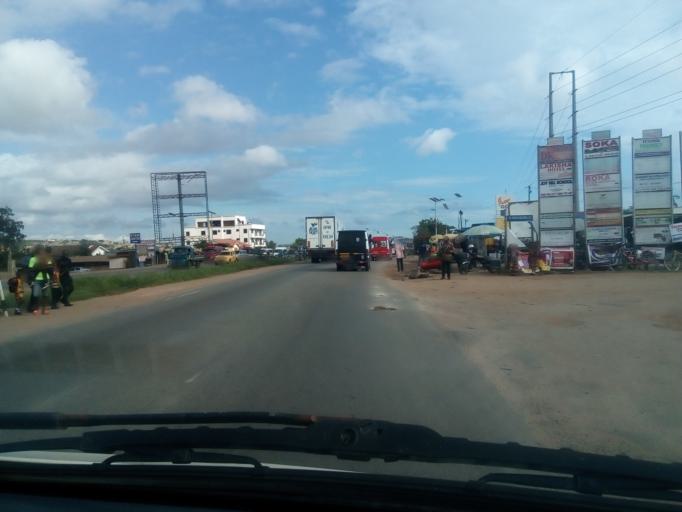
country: GH
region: Greater Accra
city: Achiaman
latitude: 5.6989
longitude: -0.2927
